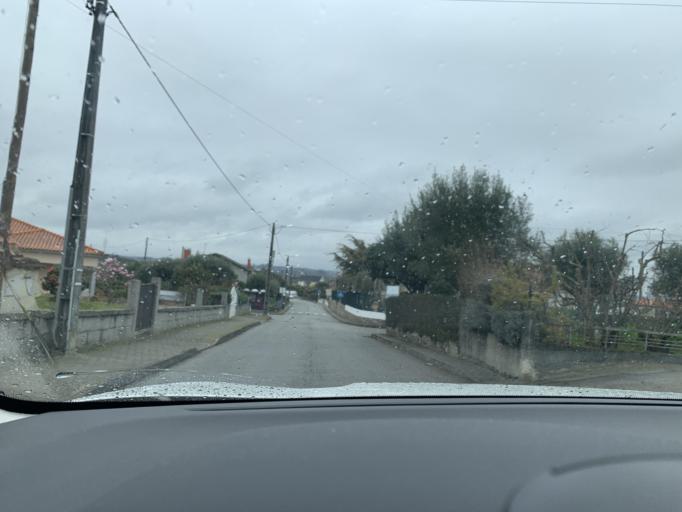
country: PT
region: Viseu
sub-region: Nelas
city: Nelas
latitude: 40.5963
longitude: -7.8425
